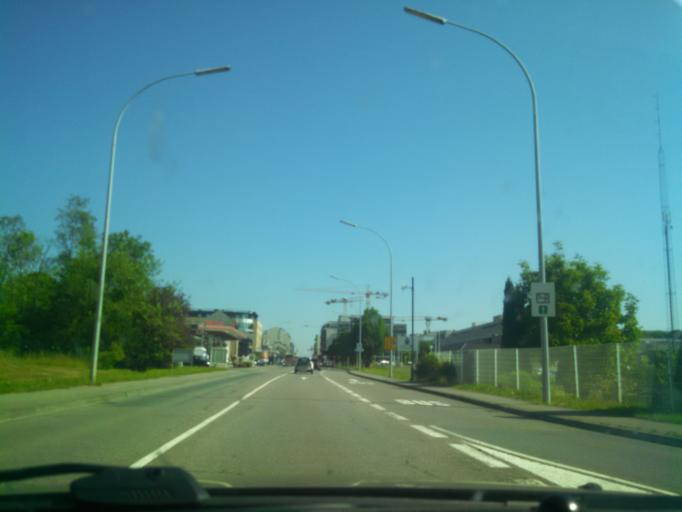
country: LU
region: Luxembourg
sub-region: Canton de Luxembourg
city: Luxembourg
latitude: 49.5877
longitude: 6.1161
